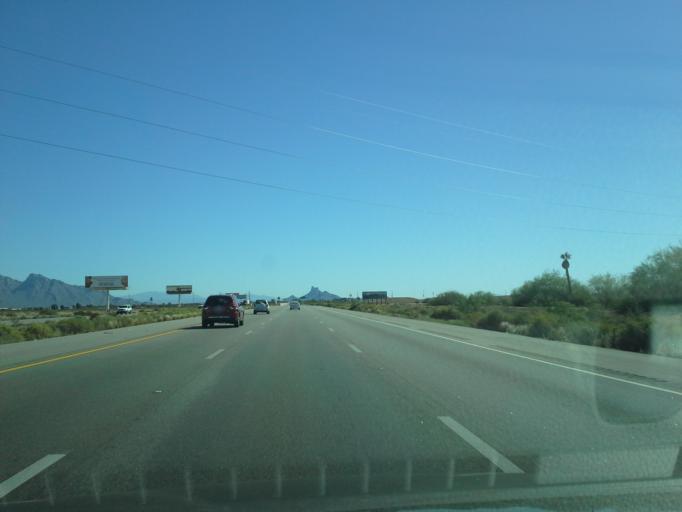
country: US
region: Arizona
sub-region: Pinal County
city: Eloy
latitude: 32.7450
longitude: -111.5679
